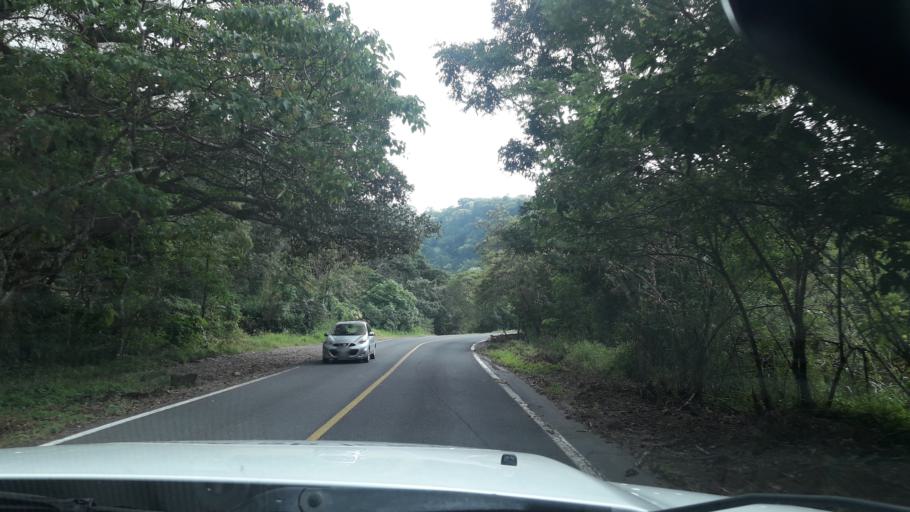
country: MX
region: Colima
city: Suchitlan
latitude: 19.4445
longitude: -103.7150
